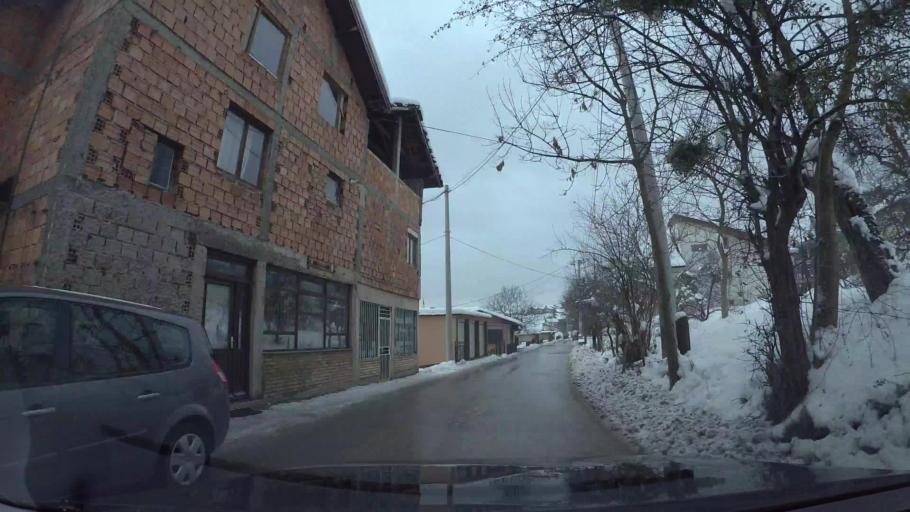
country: BA
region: Federation of Bosnia and Herzegovina
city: Kobilja Glava
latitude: 43.8732
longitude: 18.4378
